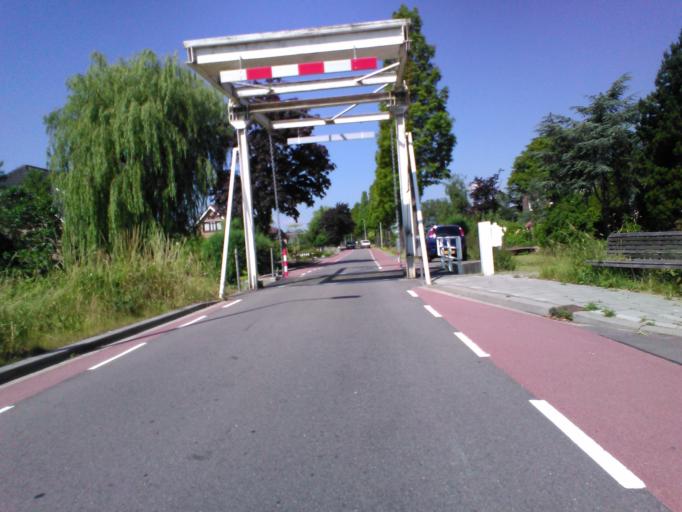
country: NL
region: South Holland
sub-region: Gemeente Boskoop
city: Boskoop
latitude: 52.0825
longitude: 4.6460
